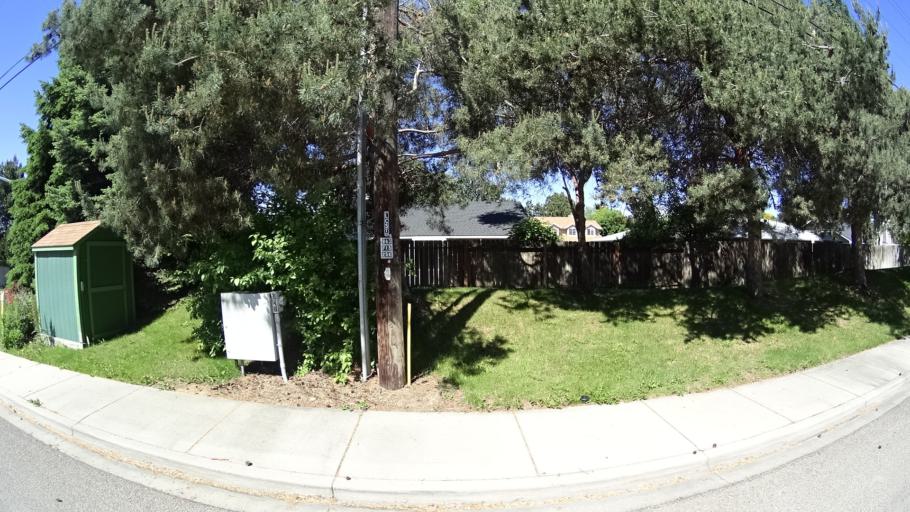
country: US
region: Idaho
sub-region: Ada County
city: Meridian
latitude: 43.6251
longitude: -116.3746
